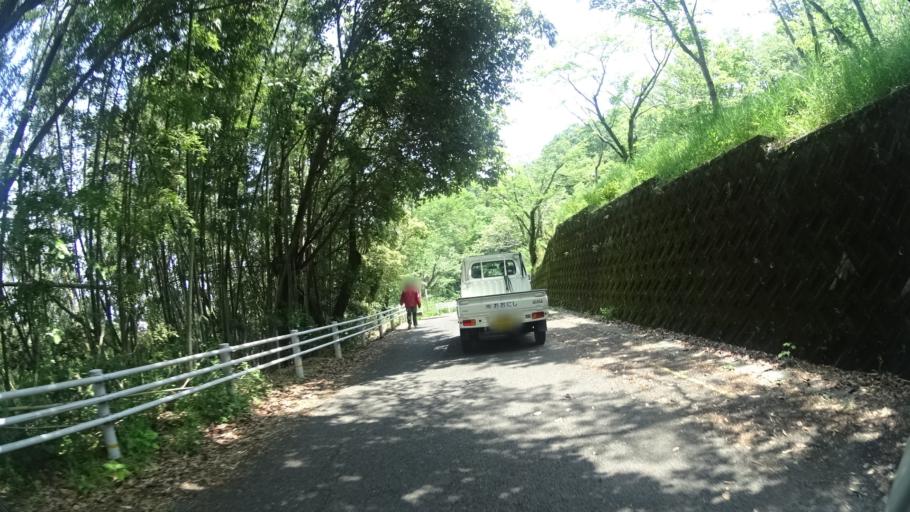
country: JP
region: Tokushima
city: Tokushima-shi
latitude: 34.0694
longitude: 134.5122
